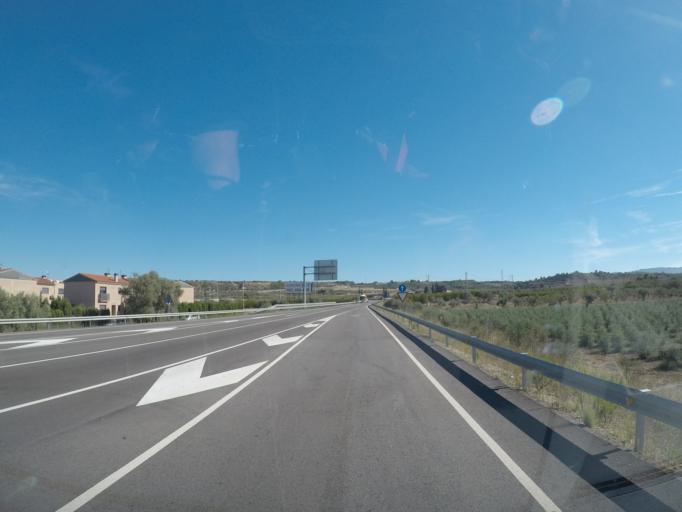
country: ES
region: Catalonia
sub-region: Provincia de Tarragona
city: Garcia
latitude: 41.0956
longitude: 0.6545
